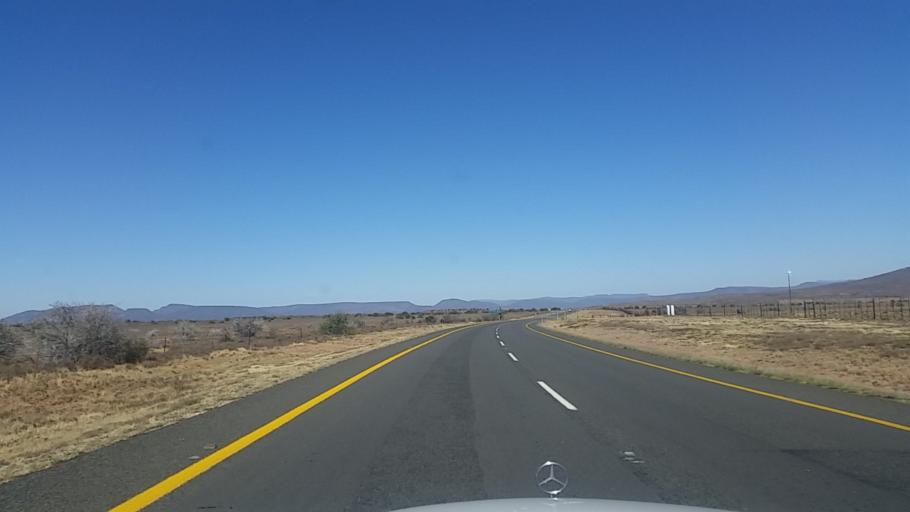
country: ZA
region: Eastern Cape
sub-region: Cacadu District Municipality
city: Graaff-Reinet
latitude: -32.1315
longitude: 24.5861
